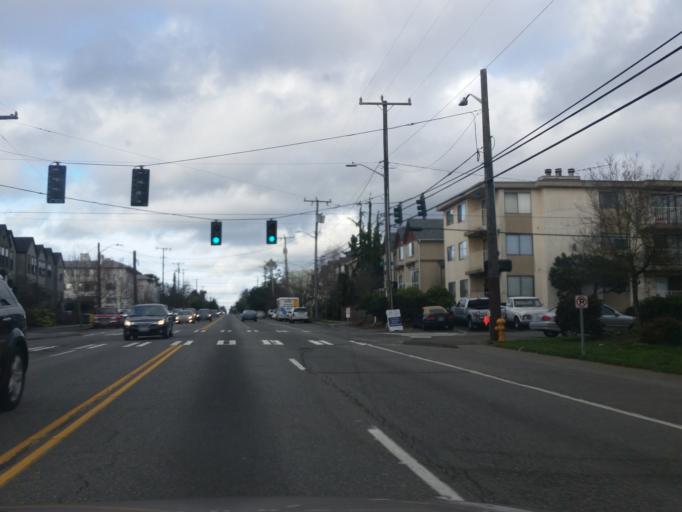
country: US
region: Washington
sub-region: King County
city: Shoreline
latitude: 47.7138
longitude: -122.3555
